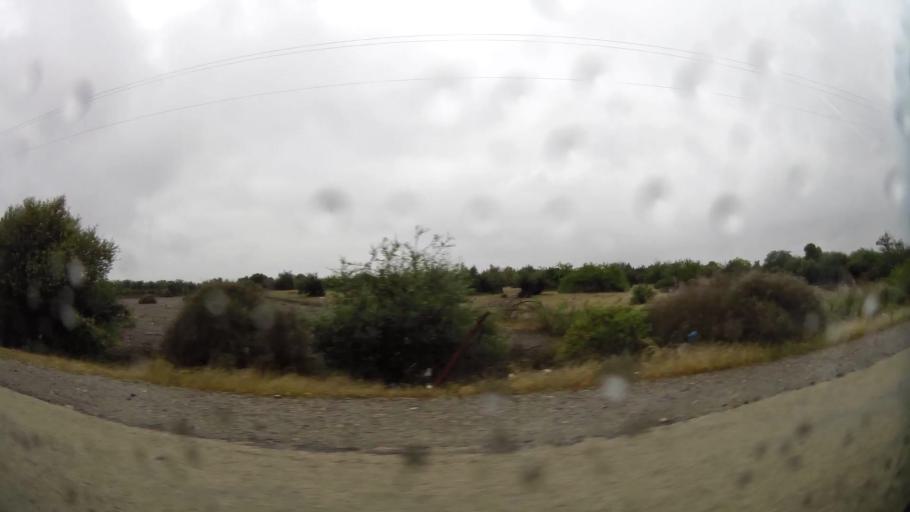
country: MA
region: Taza-Al Hoceima-Taounate
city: Imzourene
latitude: 35.1366
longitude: -3.7834
